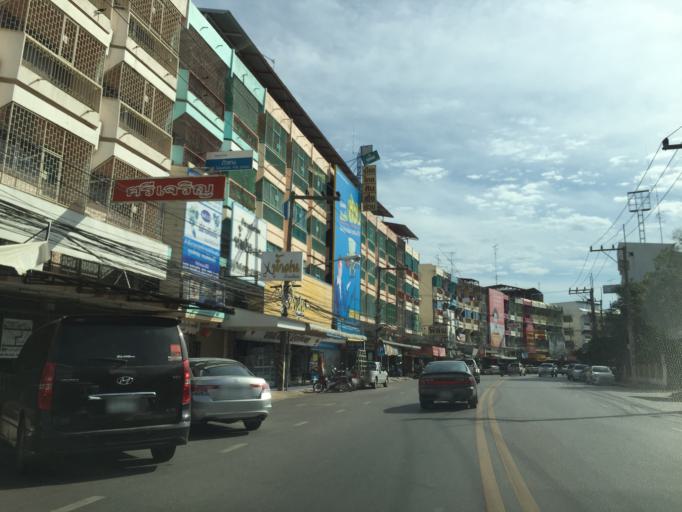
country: TH
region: Phitsanulok
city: Phitsanulok
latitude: 16.8205
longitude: 100.2685
